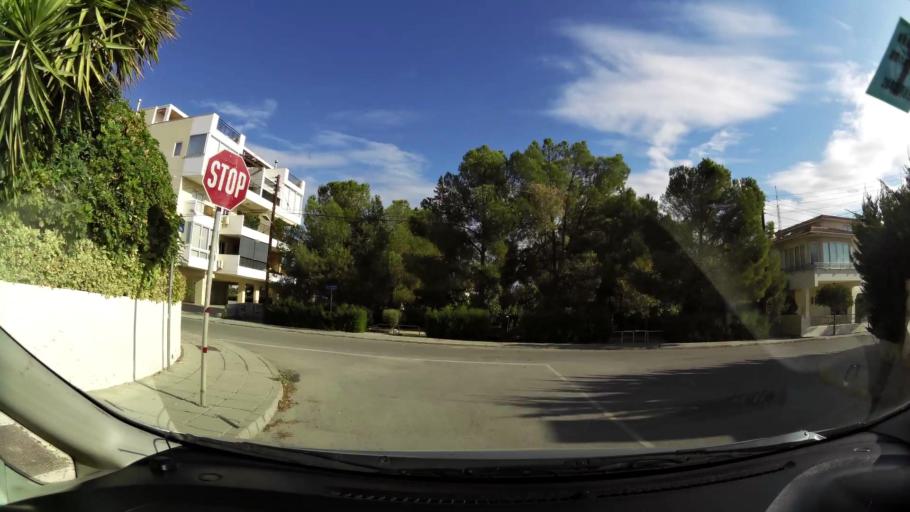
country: CY
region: Lefkosia
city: Nicosia
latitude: 35.1355
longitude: 33.3629
